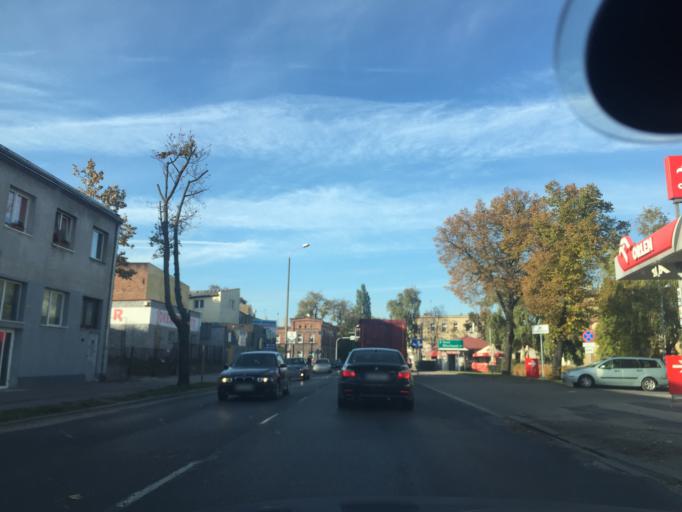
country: PL
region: Kujawsko-Pomorskie
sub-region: Powiat inowroclawski
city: Inowroclaw
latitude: 52.7952
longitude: 18.2651
